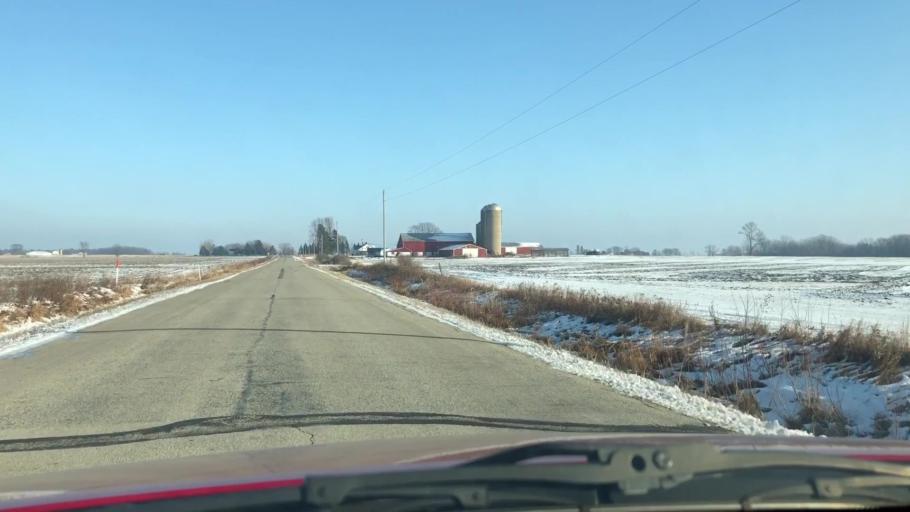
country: US
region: Wisconsin
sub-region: Outagamie County
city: Seymour
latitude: 44.4870
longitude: -88.3286
